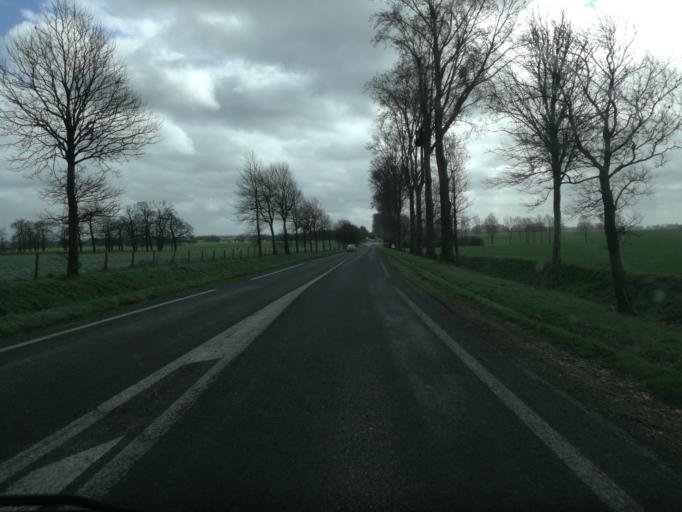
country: FR
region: Haute-Normandie
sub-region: Departement de la Seine-Maritime
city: Fauville-en-Caux
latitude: 49.6377
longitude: 0.6264
